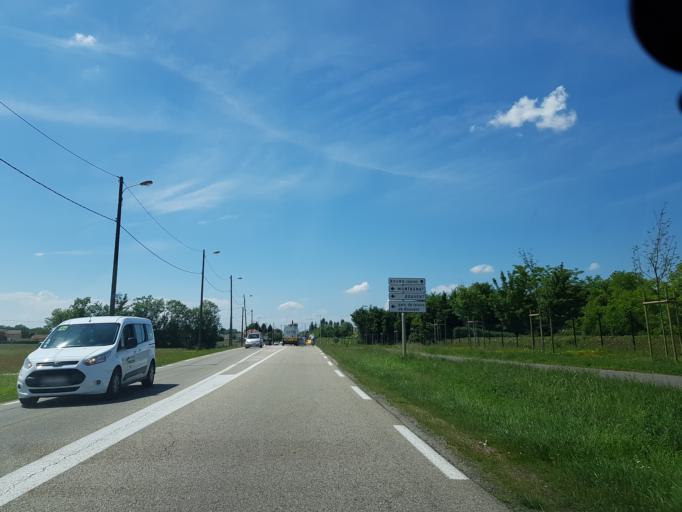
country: FR
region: Rhone-Alpes
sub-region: Departement de l'Ain
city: Montagnat
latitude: 46.1958
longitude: 5.2679
